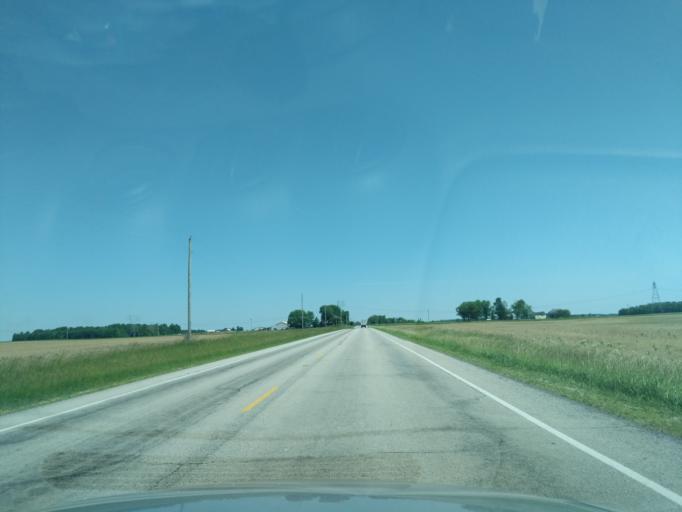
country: US
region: Indiana
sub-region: Huntington County
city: Huntington
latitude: 40.9285
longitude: -85.4710
